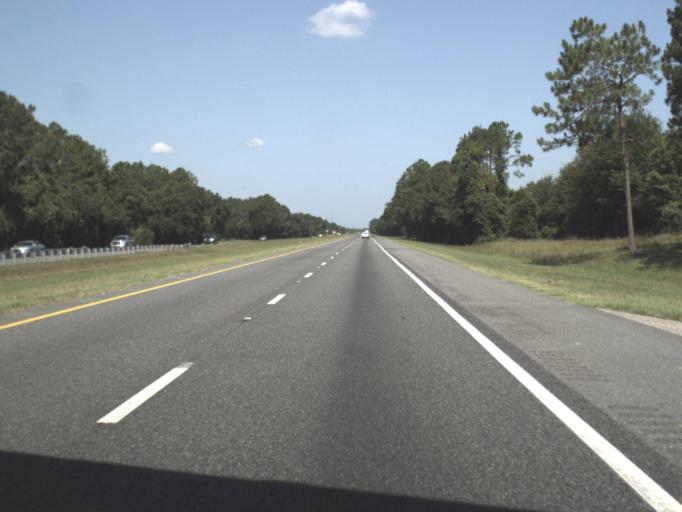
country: US
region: Florida
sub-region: Suwannee County
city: Live Oak
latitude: 30.3562
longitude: -83.1822
